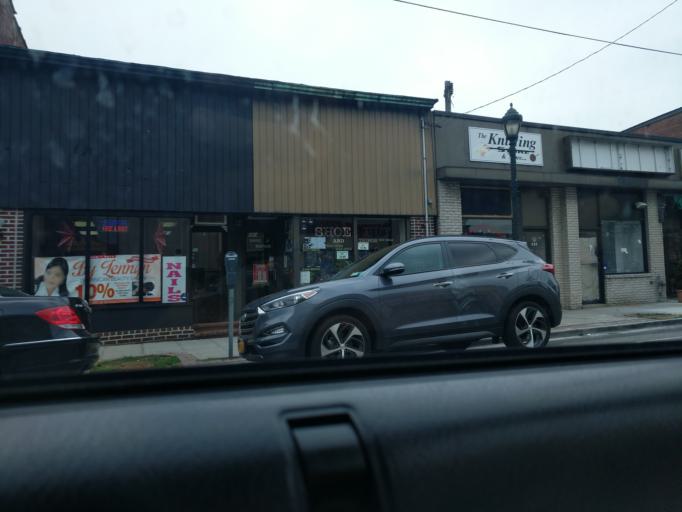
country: US
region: New York
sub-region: Nassau County
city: Valley Stream
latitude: 40.6610
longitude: -73.6997
